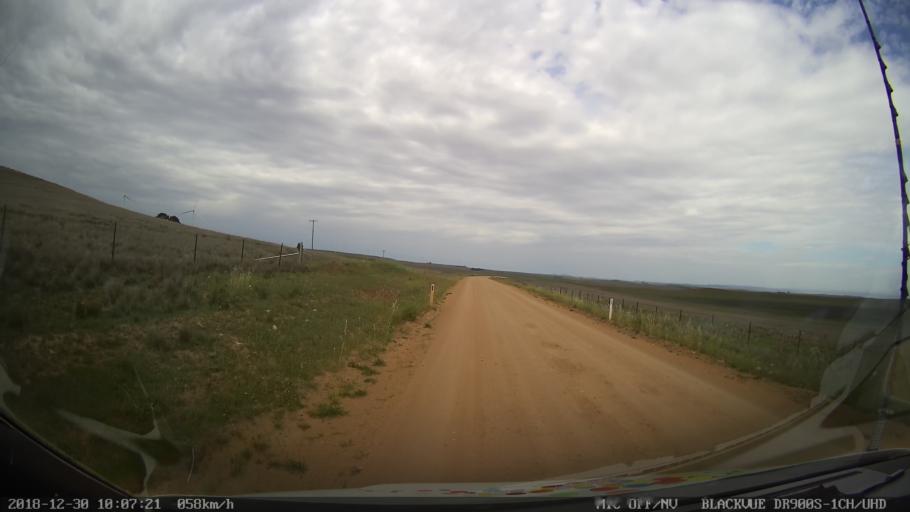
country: AU
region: New South Wales
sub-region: Cooma-Monaro
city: Cooma
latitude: -36.5389
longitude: 149.1233
